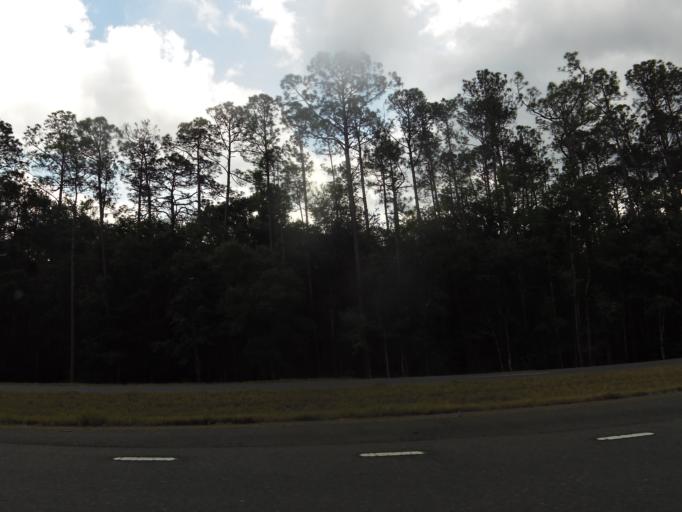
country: US
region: Georgia
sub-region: Charlton County
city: Folkston
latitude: 30.8501
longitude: -81.9494
